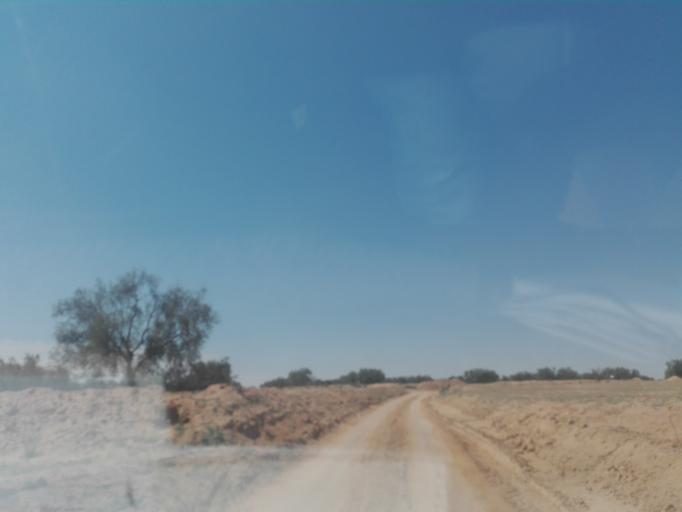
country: TN
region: Safaqis
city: Bi'r `Ali Bin Khalifah
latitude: 34.6059
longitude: 10.3490
